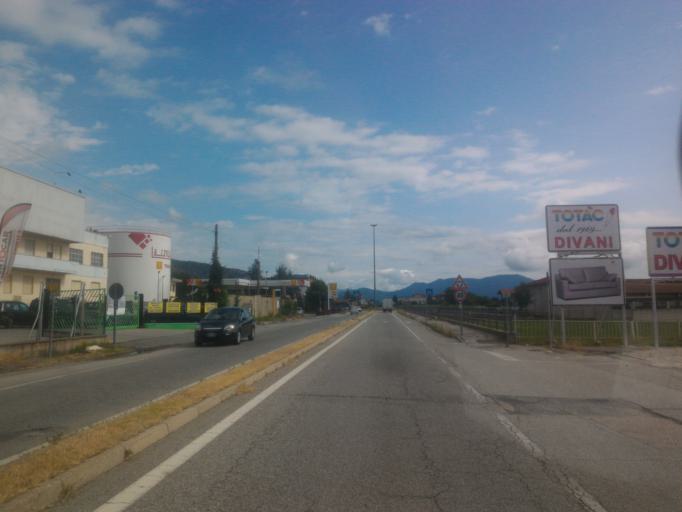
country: IT
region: Piedmont
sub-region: Provincia di Torino
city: Frossasco
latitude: 44.9170
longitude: 7.3644
